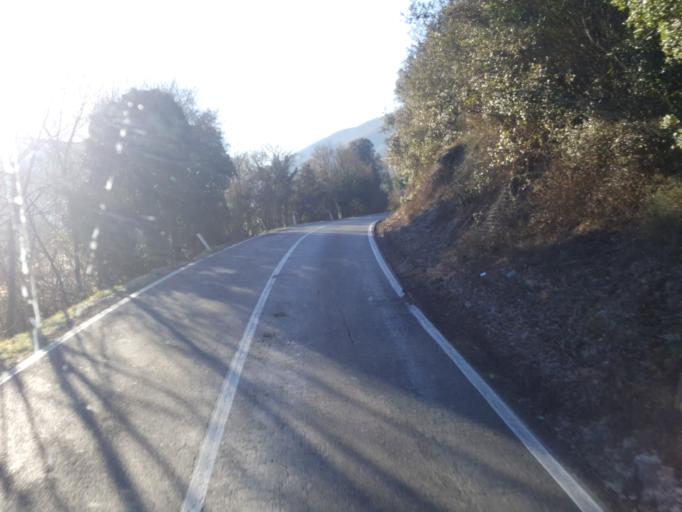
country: IT
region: Latium
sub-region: Provincia di Rieti
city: Colli sul Velino
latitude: 42.5125
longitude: 12.7394
